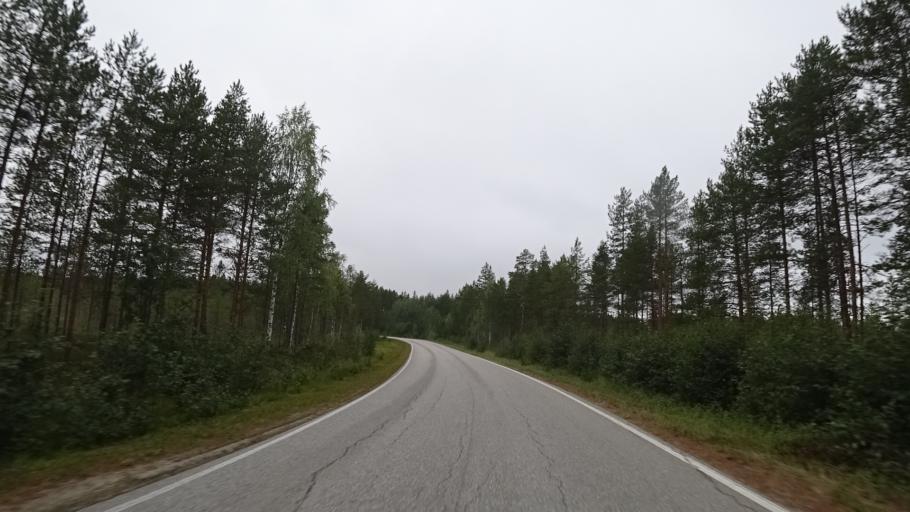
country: FI
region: North Karelia
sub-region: Pielisen Karjala
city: Lieksa
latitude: 63.3595
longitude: 30.2638
